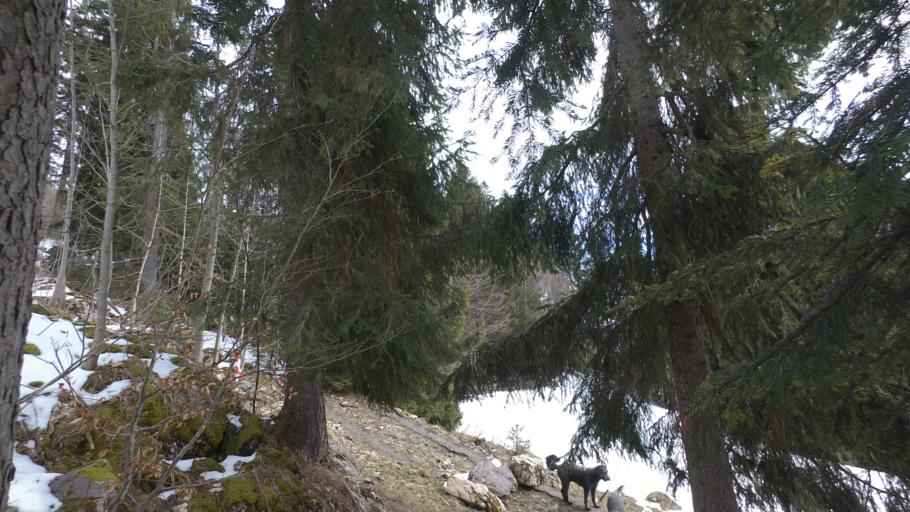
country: DE
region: Bavaria
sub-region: Upper Bavaria
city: Reit im Winkl
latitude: 47.6953
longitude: 12.4494
